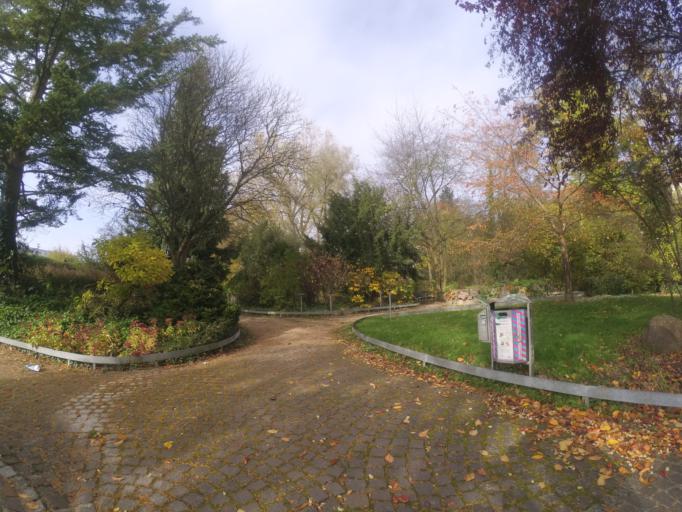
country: DE
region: Baden-Wuerttemberg
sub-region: Tuebingen Region
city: Ulm
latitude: 48.3947
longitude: 9.9871
